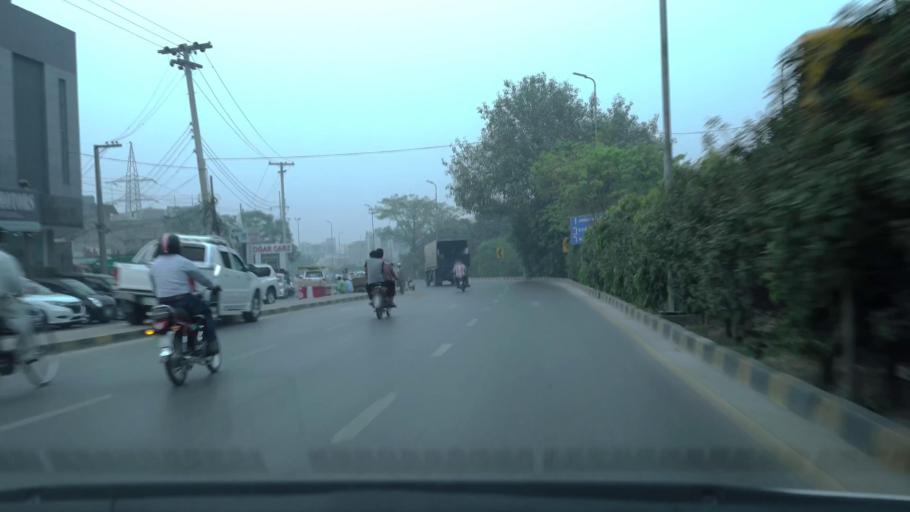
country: PK
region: Punjab
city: Lahore
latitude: 31.4767
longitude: 74.3014
